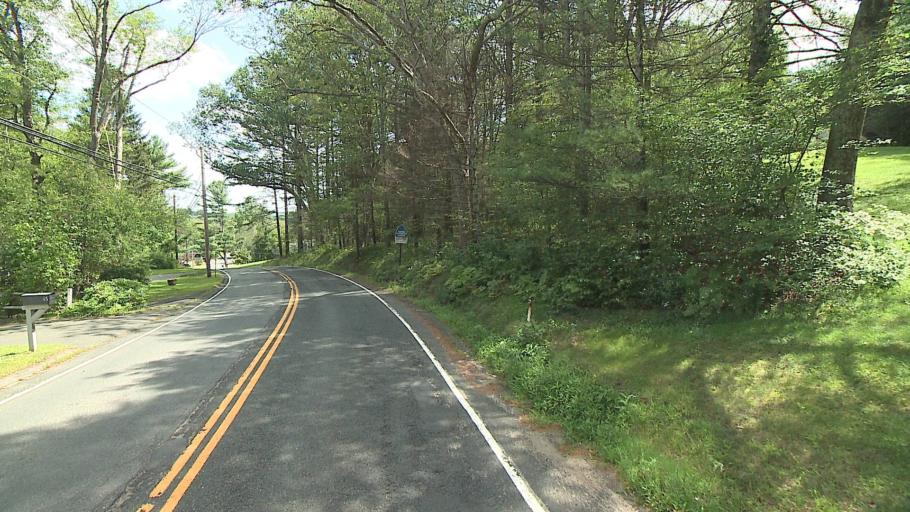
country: US
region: Connecticut
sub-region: Tolland County
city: Stafford Springs
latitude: 41.9533
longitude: -72.3246
